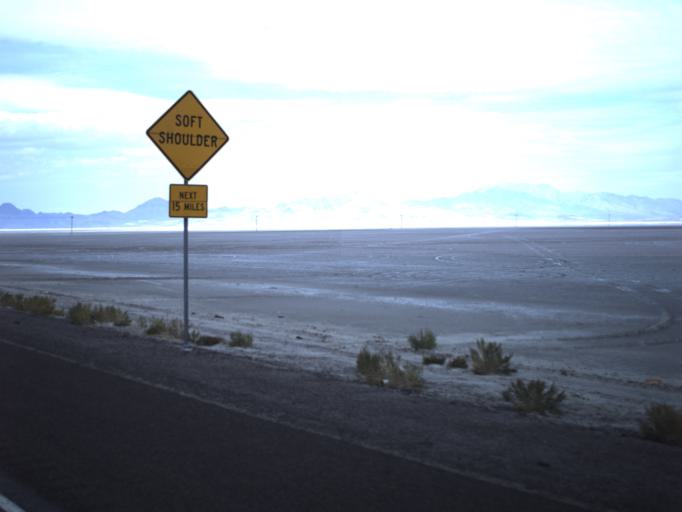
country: US
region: Utah
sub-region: Tooele County
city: Wendover
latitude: 40.7375
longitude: -113.7603
